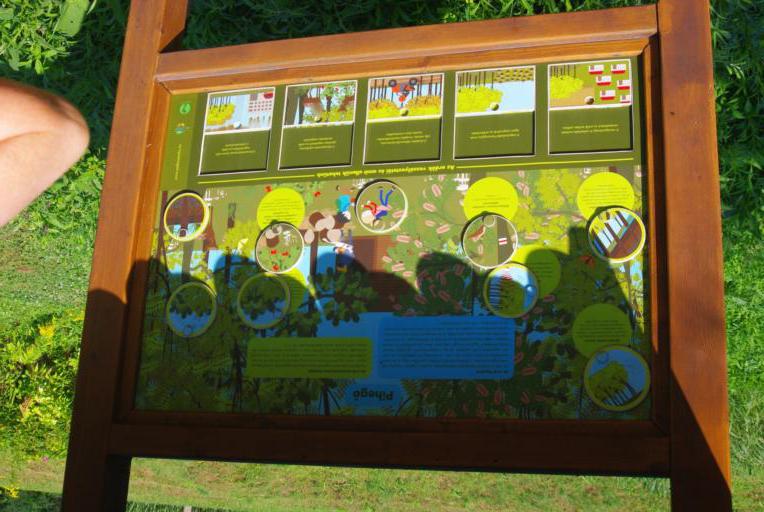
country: HU
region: Bacs-Kiskun
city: Baja
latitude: 46.1790
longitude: 18.9302
